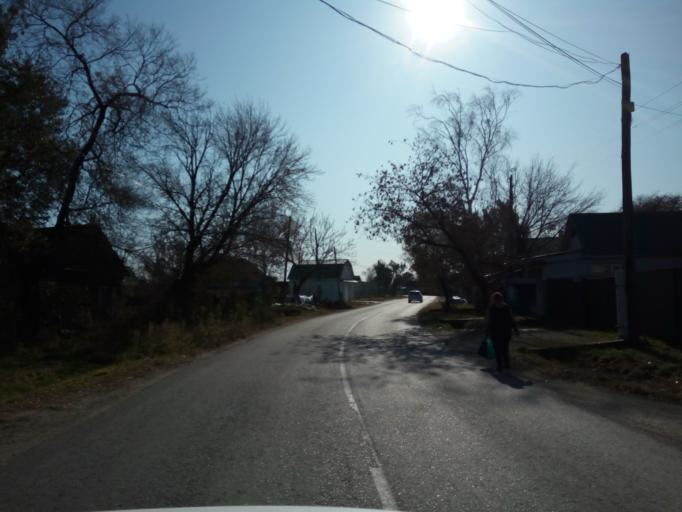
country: RU
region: Primorskiy
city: Dal'nerechensk
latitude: 45.9379
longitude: 133.7026
